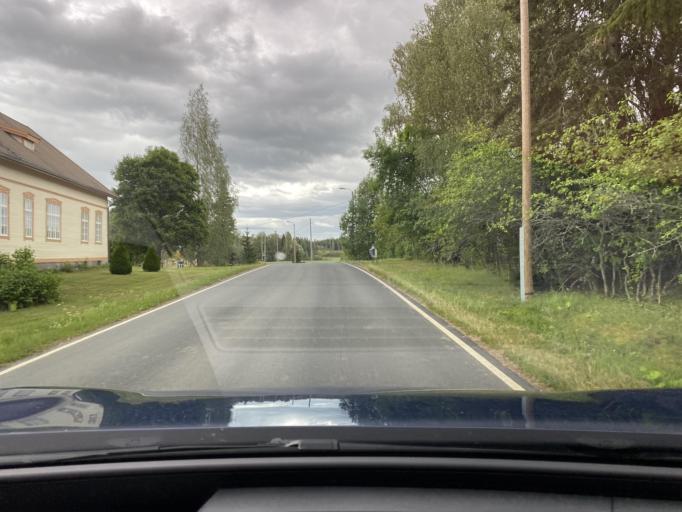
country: FI
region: Pirkanmaa
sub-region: Lounais-Pirkanmaa
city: Punkalaidun
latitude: 61.2316
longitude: 23.1330
